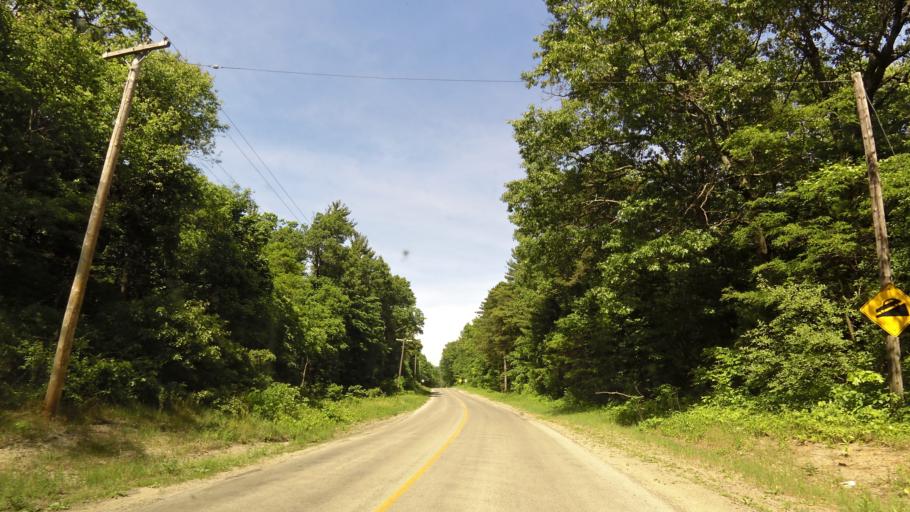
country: CA
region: Ontario
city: Norfolk County
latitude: 42.7073
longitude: -80.3243
